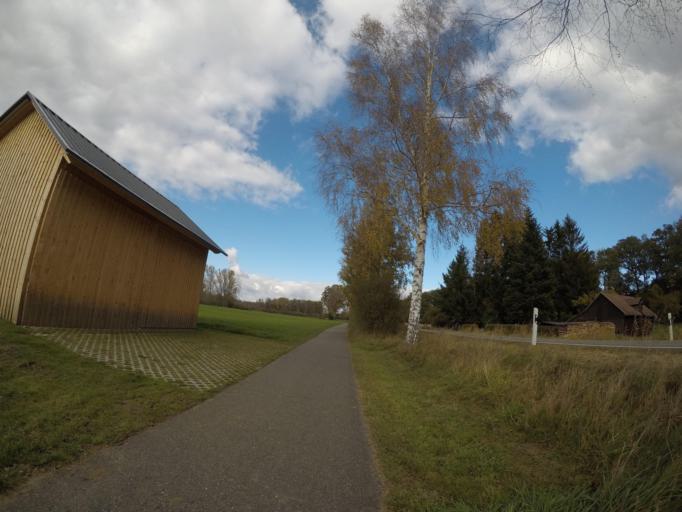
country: DE
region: Baden-Wuerttemberg
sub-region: Tuebingen Region
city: Seekirch
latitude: 48.0933
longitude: 9.6507
